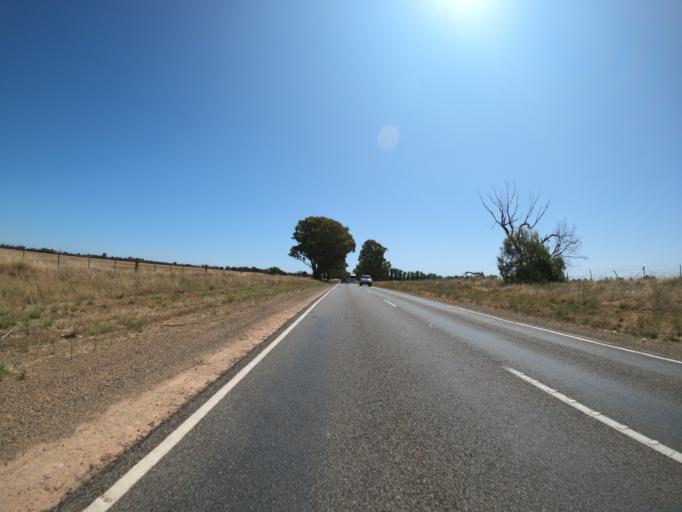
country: AU
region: Victoria
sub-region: Moira
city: Yarrawonga
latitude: -36.0252
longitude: 146.1005
